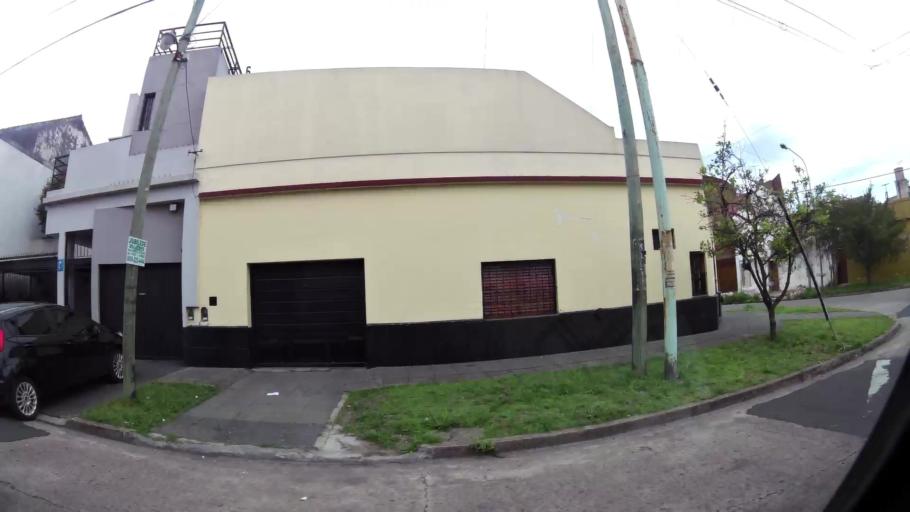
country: AR
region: Buenos Aires
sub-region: Partido de Lanus
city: Lanus
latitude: -34.6774
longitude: -58.3971
